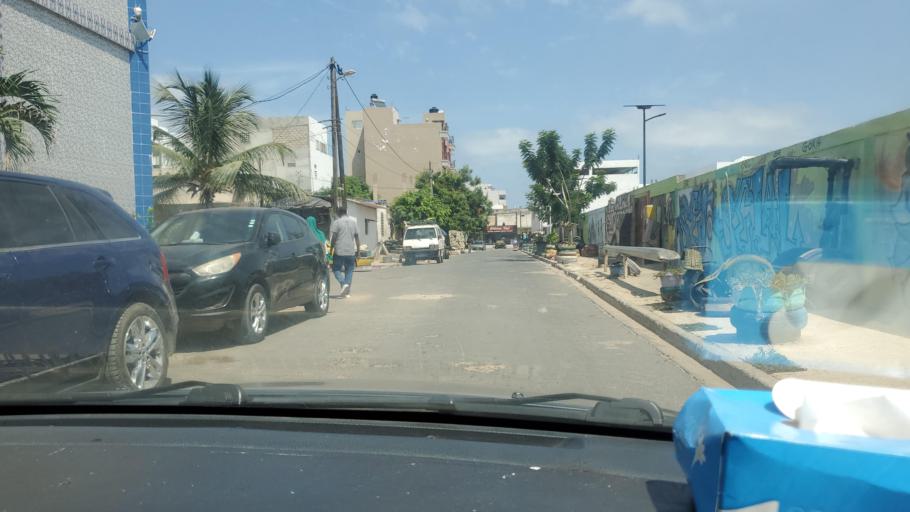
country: SN
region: Dakar
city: Grand Dakar
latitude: 14.7250
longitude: -17.4512
